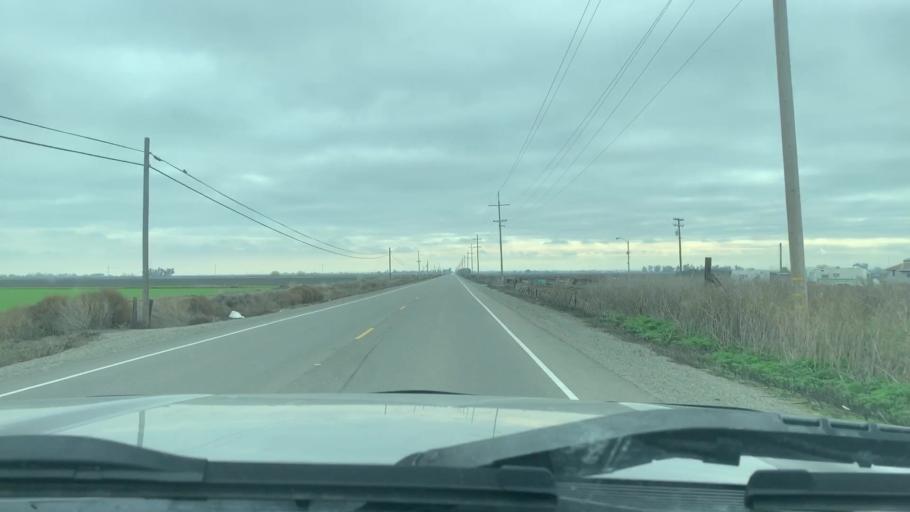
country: US
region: California
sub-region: Merced County
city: Los Banos
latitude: 37.1274
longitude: -120.8348
